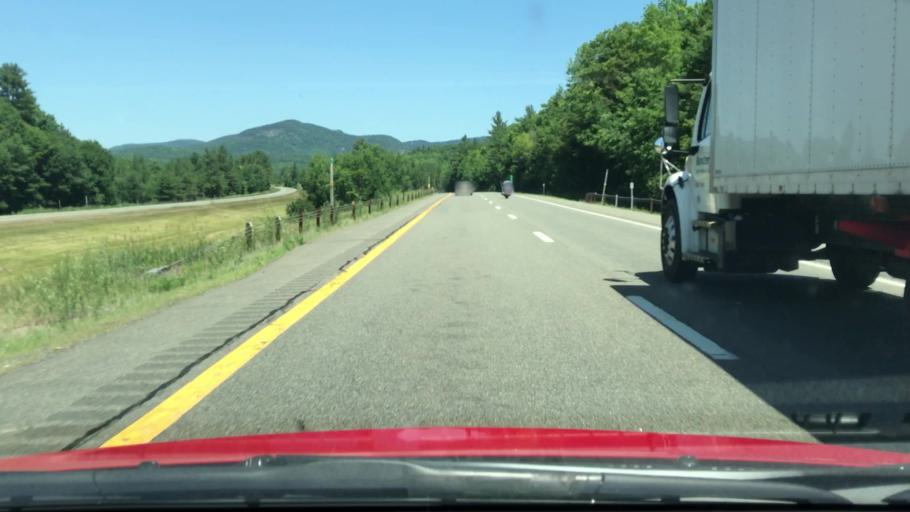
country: US
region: New York
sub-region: Essex County
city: Elizabethtown
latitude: 44.3387
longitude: -73.5329
